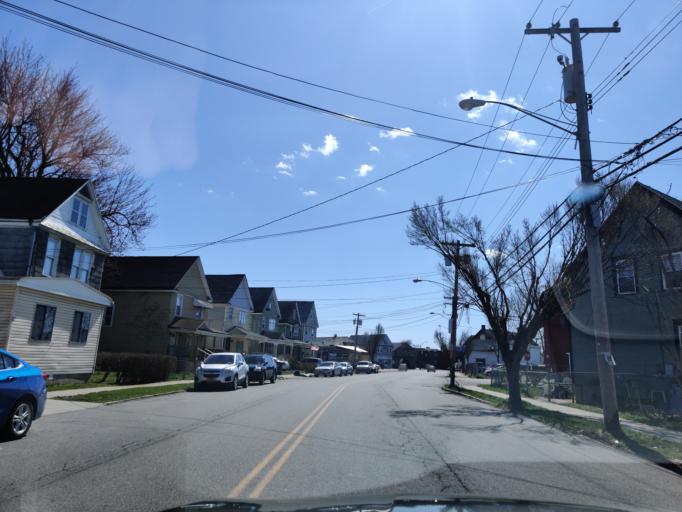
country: US
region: New York
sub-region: Erie County
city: Kenmore
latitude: 42.9384
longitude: -78.8927
